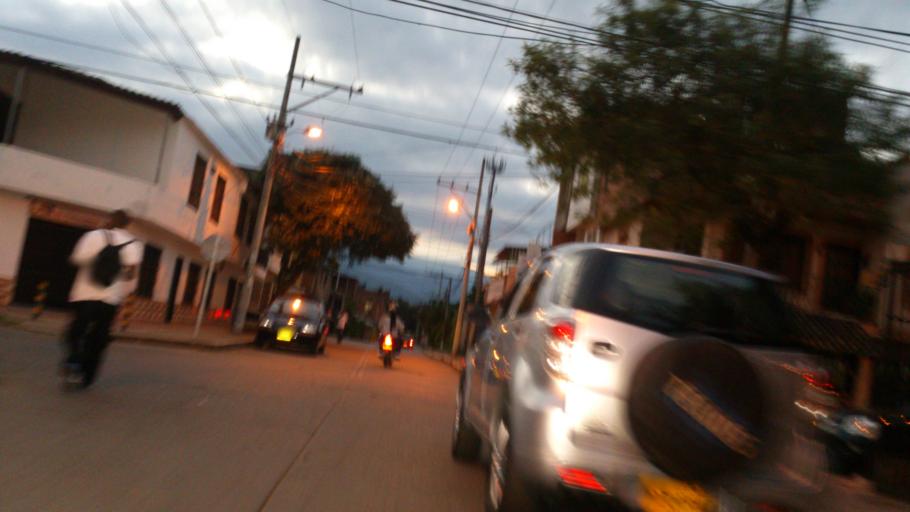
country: CO
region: Valle del Cauca
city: Jamundi
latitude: 3.2642
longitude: -76.5401
